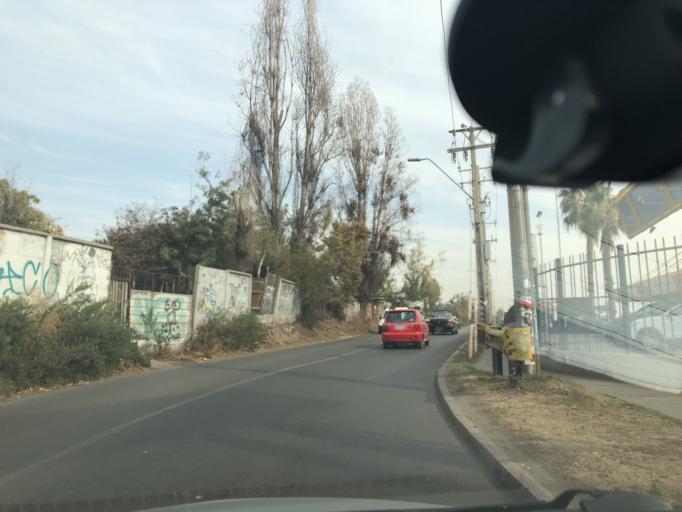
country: CL
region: Santiago Metropolitan
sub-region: Provincia de Cordillera
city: Puente Alto
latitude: -33.5716
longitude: -70.5566
